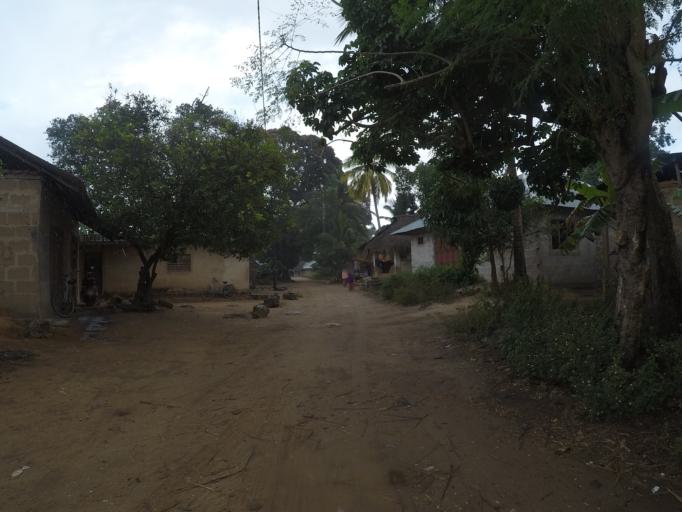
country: TZ
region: Zanzibar North
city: Mkokotoni
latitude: -5.9533
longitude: 39.1950
